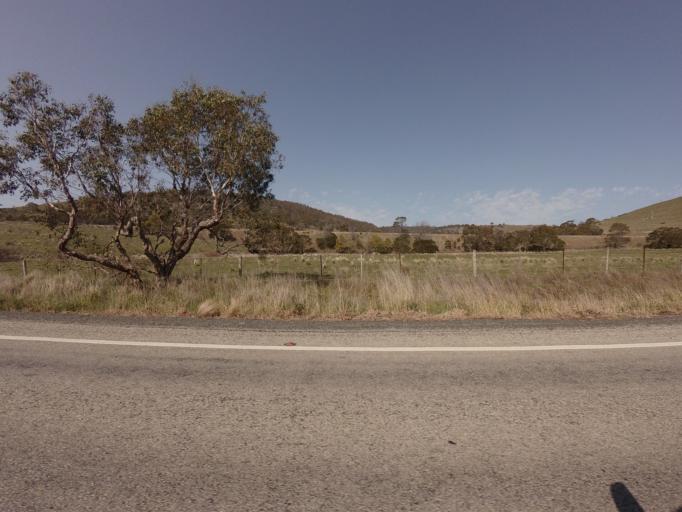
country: AU
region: Tasmania
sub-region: Northern Midlands
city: Evandale
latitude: -41.8178
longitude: 147.5479
